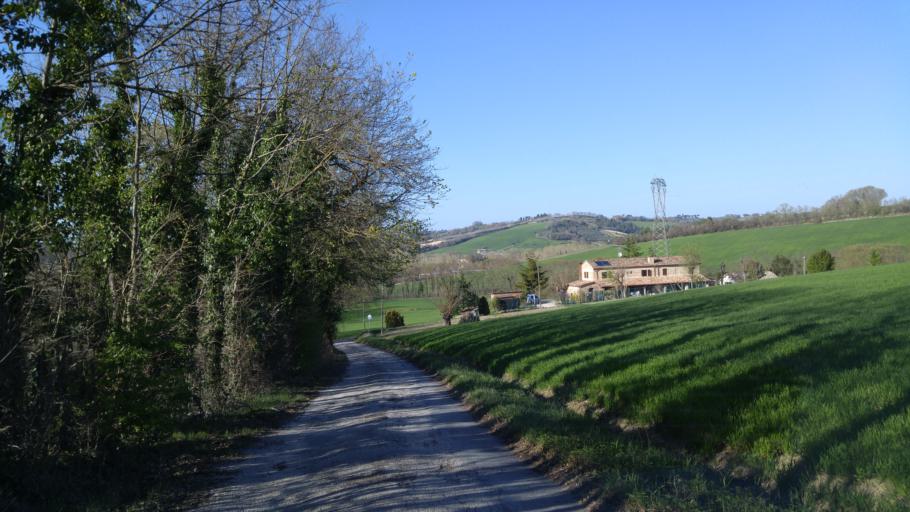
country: IT
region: The Marches
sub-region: Provincia di Pesaro e Urbino
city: Cuccurano
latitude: 43.8216
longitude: 12.9155
